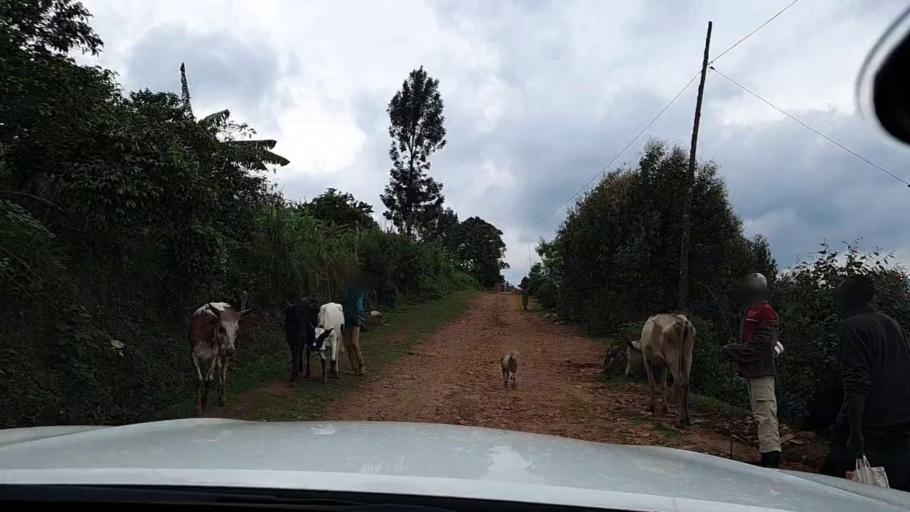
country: RW
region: Western Province
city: Kibuye
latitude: -2.1887
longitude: 29.2986
